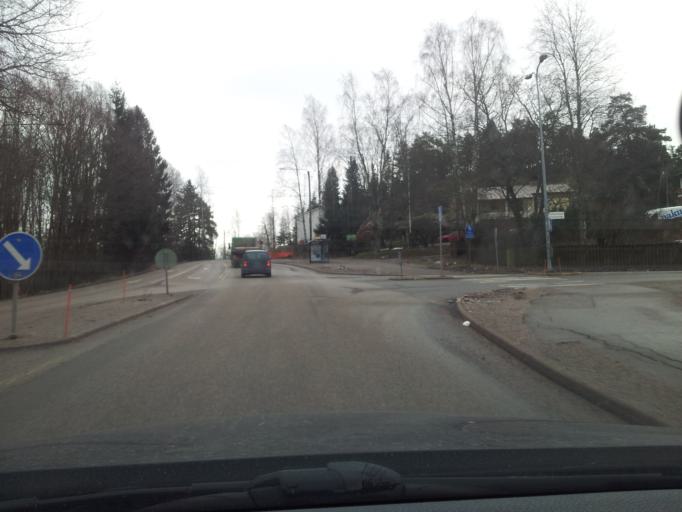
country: FI
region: Uusimaa
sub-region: Helsinki
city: Kauniainen
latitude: 60.1695
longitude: 24.6942
